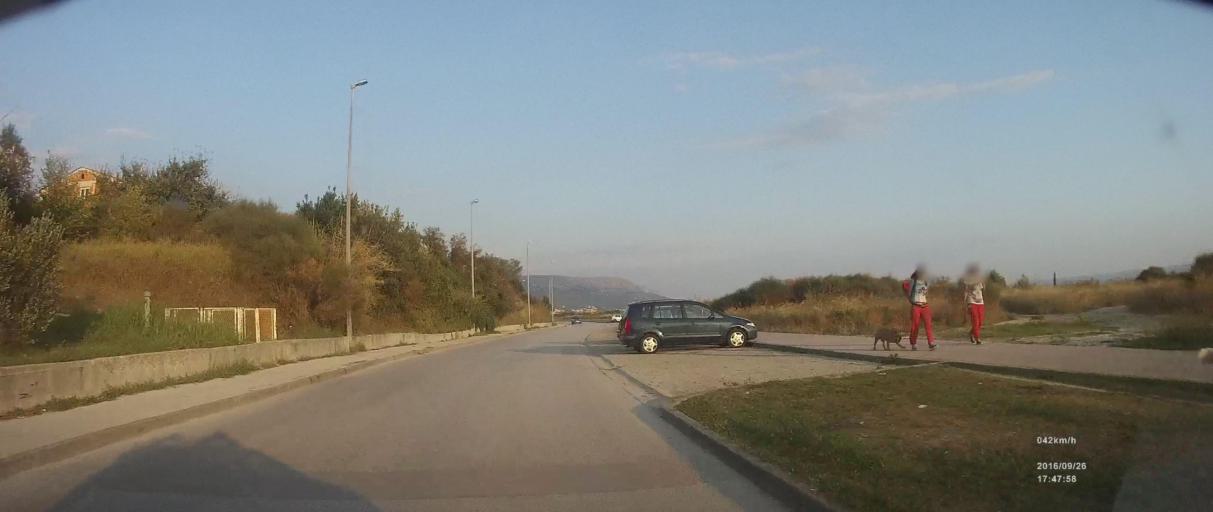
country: HR
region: Splitsko-Dalmatinska
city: Kamen
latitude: 43.5021
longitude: 16.4869
